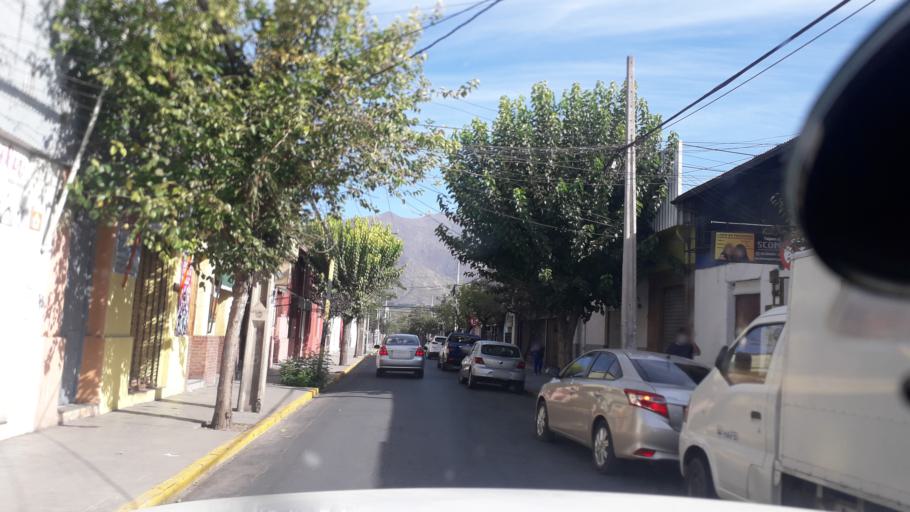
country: CL
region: Valparaiso
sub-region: Provincia de San Felipe
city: San Felipe
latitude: -32.7510
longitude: -70.7273
